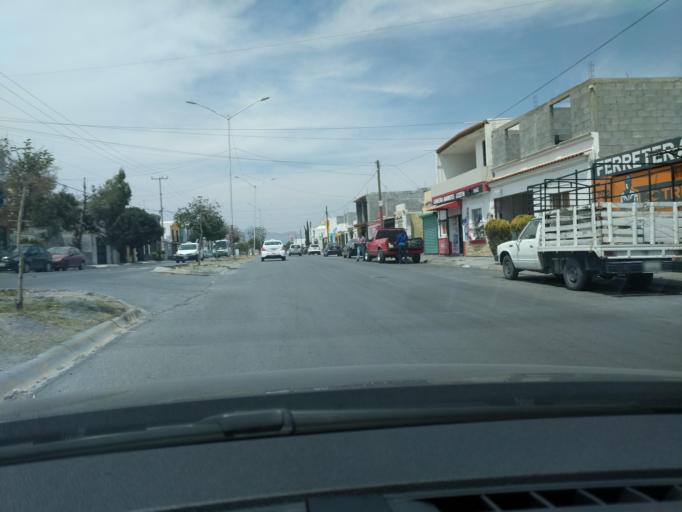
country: MX
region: Coahuila
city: Saltillo
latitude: 25.3539
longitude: -101.0152
